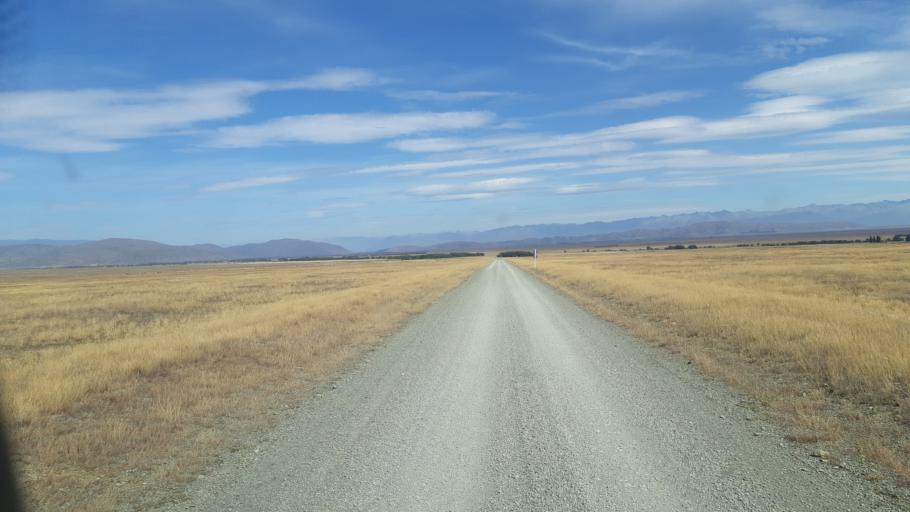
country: NZ
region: Canterbury
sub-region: Timaru District
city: Pleasant Point
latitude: -44.1949
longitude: 170.5395
